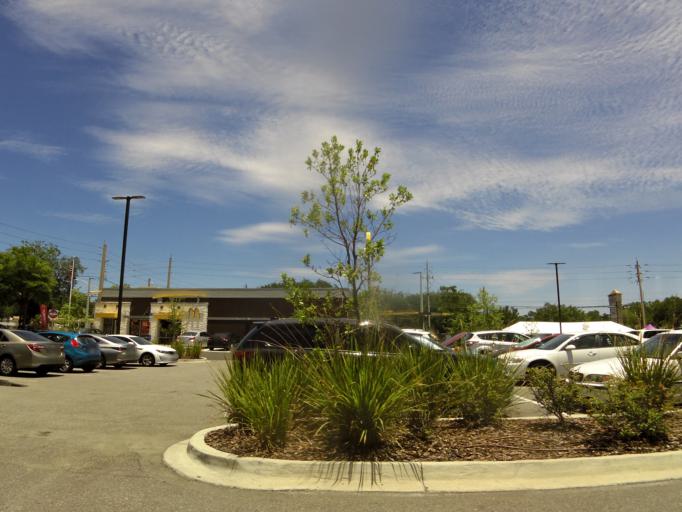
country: US
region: Florida
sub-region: Saint Johns County
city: Fruit Cove
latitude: 30.1605
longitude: -81.6336
